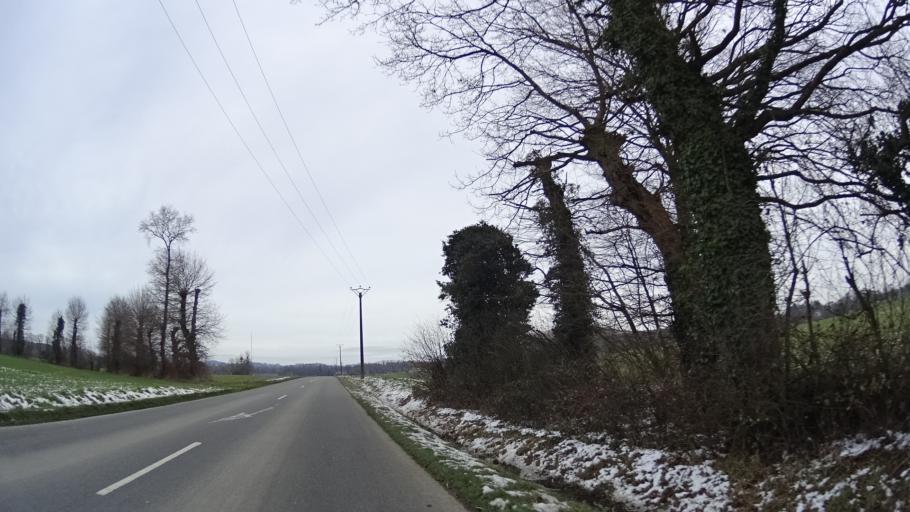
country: FR
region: Brittany
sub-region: Departement d'Ille-et-Vilaine
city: Irodouer
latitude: 48.2619
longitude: -1.9853
